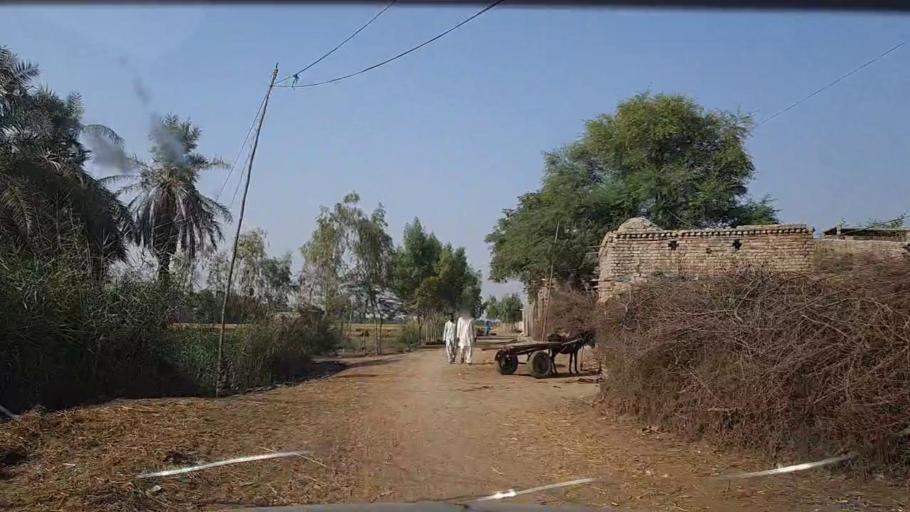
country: PK
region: Sindh
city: Shikarpur
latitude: 28.1208
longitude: 68.5786
